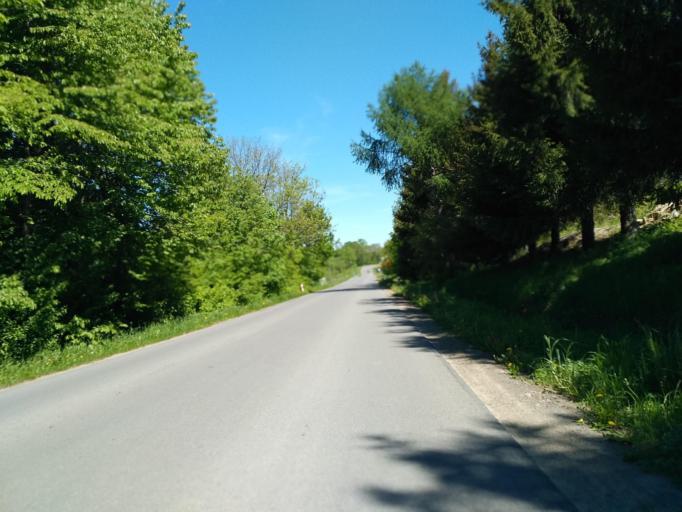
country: PL
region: Subcarpathian Voivodeship
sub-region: Powiat sanocki
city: Nowosielce-Gniewosz
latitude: 49.5371
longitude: 22.0559
